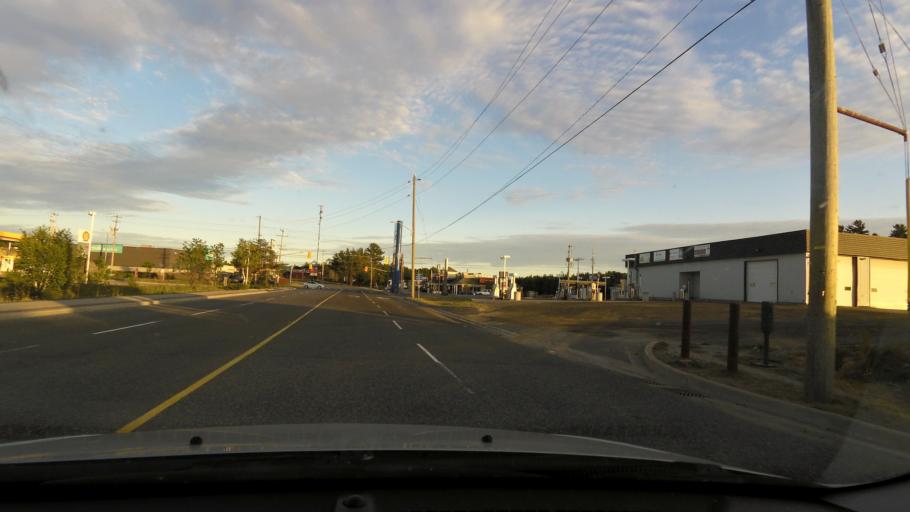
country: CA
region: Ontario
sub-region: Parry Sound District
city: Parry Sound
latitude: 45.3451
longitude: -80.0108
